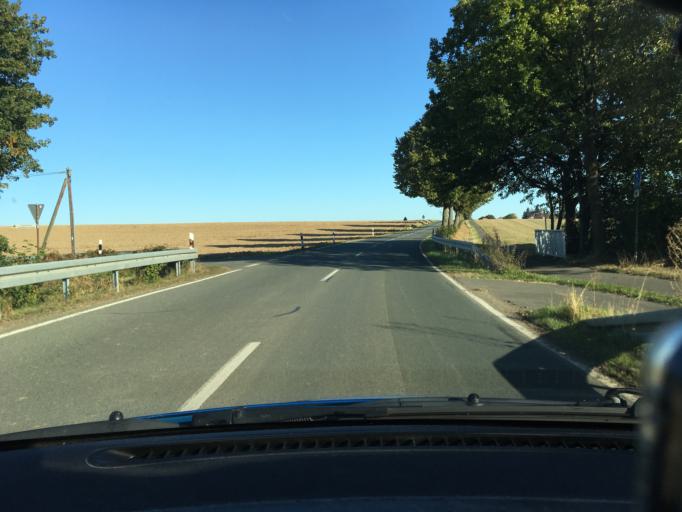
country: DE
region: Lower Saxony
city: Hulsede
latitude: 52.2331
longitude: 9.3749
